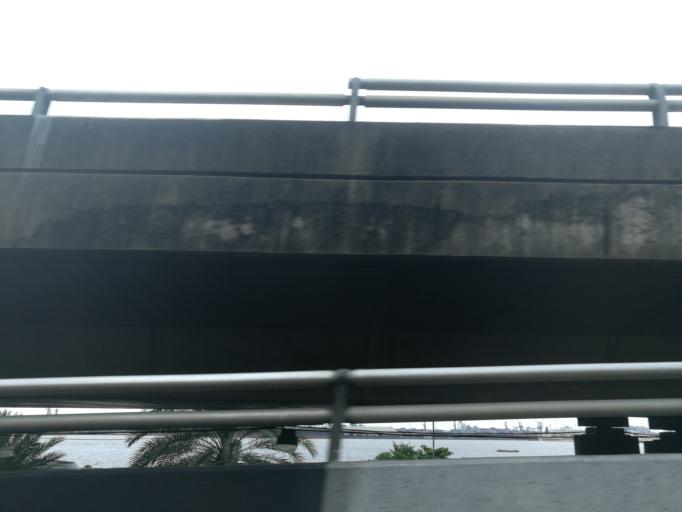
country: NG
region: Lagos
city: Lagos
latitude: 6.4458
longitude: 3.3961
